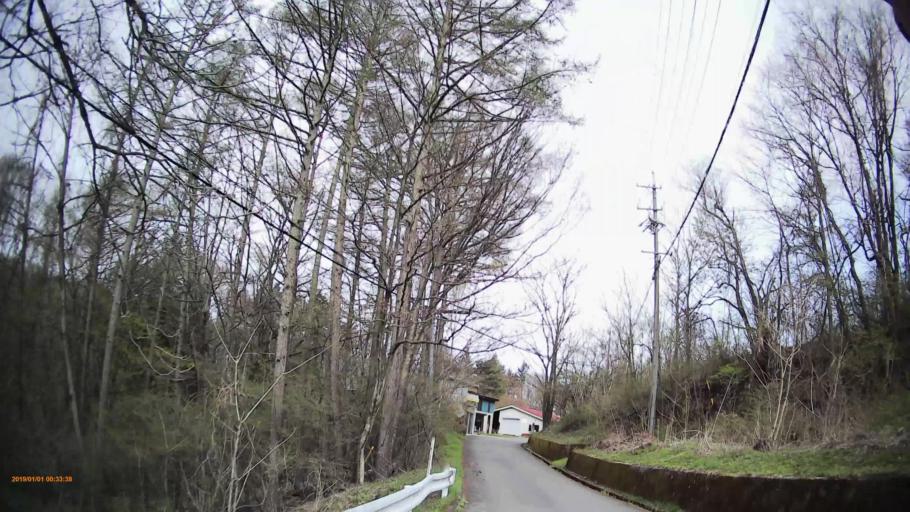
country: JP
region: Nagano
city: Chino
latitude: 35.9333
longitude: 138.2028
